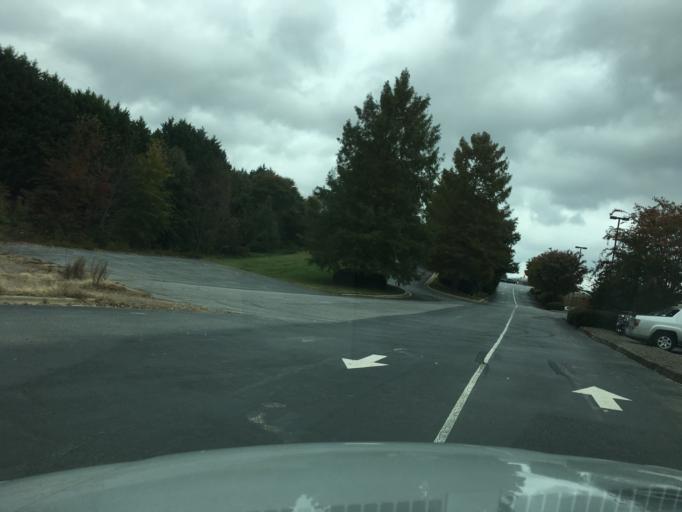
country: US
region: North Carolina
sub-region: Catawba County
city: Hickory
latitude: 35.7021
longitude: -81.2995
